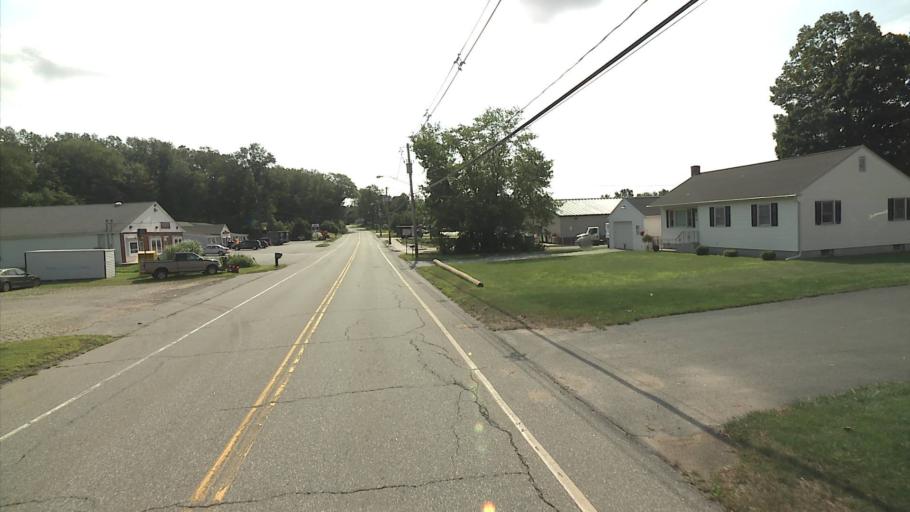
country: US
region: Connecticut
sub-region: New London County
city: Colchester
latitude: 41.5802
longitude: -72.3470
